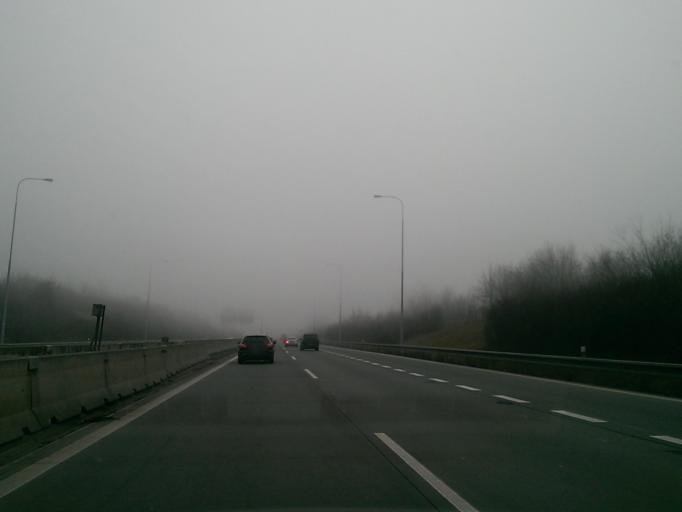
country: CZ
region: Olomoucky
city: Hnevotin
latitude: 49.5631
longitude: 17.2205
